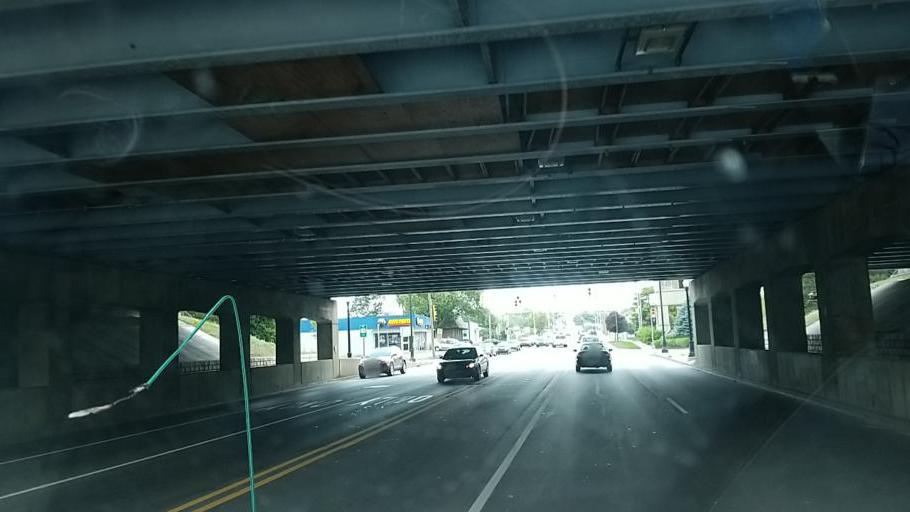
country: US
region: Michigan
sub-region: Kent County
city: Grand Rapids
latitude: 42.9848
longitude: -85.6773
